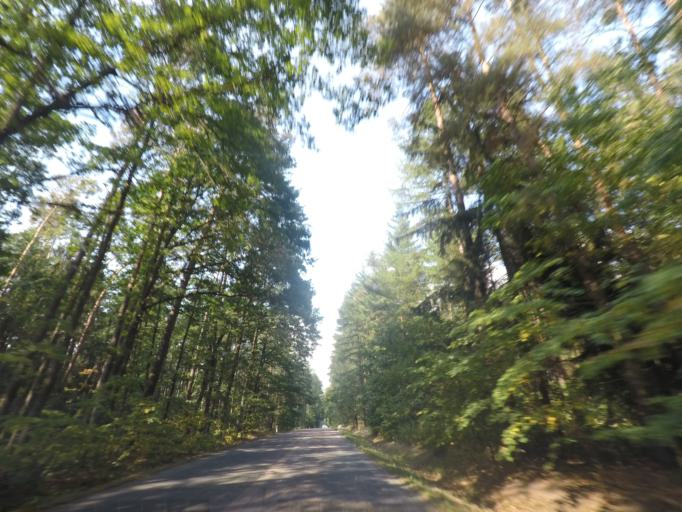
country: CZ
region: Pardubicky
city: Horni Jeleni
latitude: 50.0360
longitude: 16.0823
